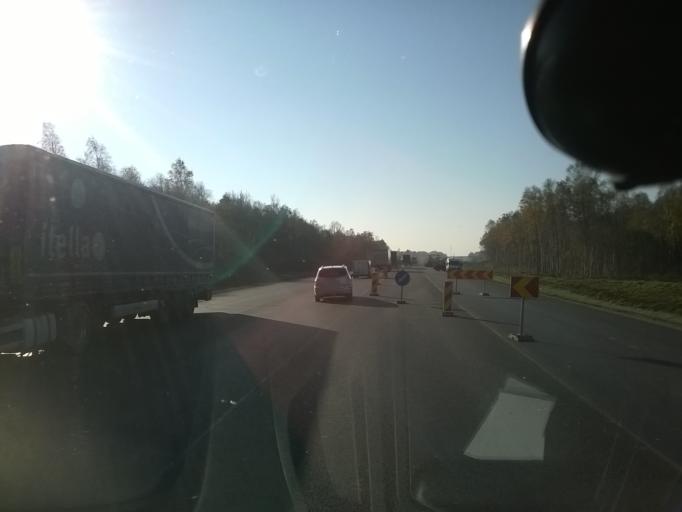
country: EE
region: Harju
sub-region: Rae vald
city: Jueri
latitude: 59.3798
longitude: 24.9169
